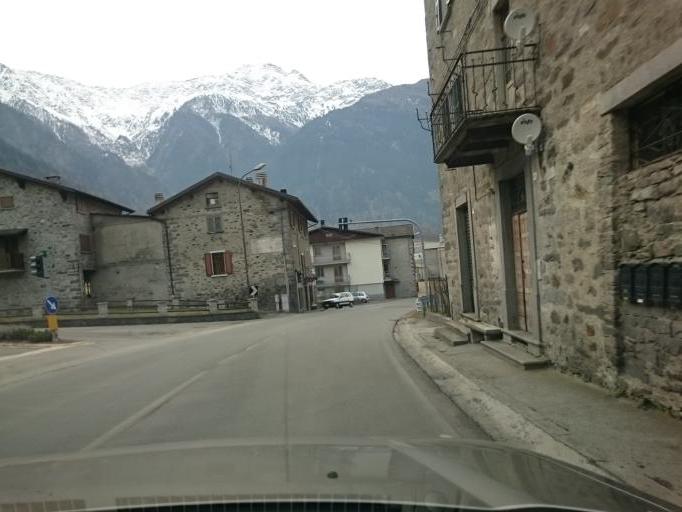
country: IT
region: Lombardy
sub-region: Provincia di Sondrio
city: Sondalo
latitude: 46.3327
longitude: 10.3494
